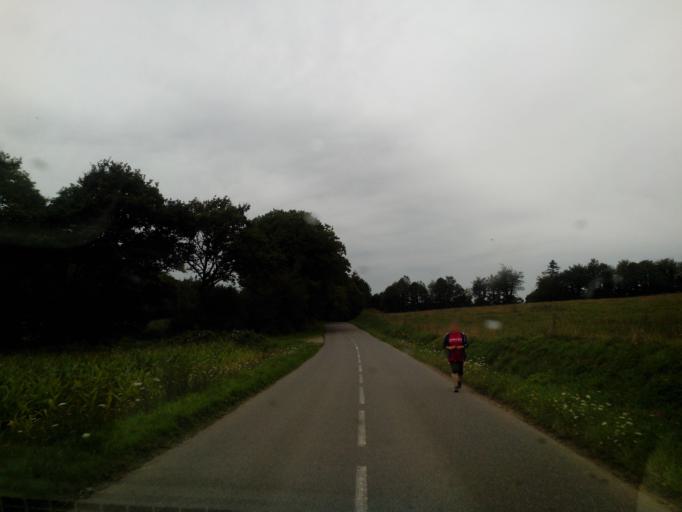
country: FR
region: Brittany
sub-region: Departement du Finistere
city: Arzano
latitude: 47.9400
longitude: -3.4428
